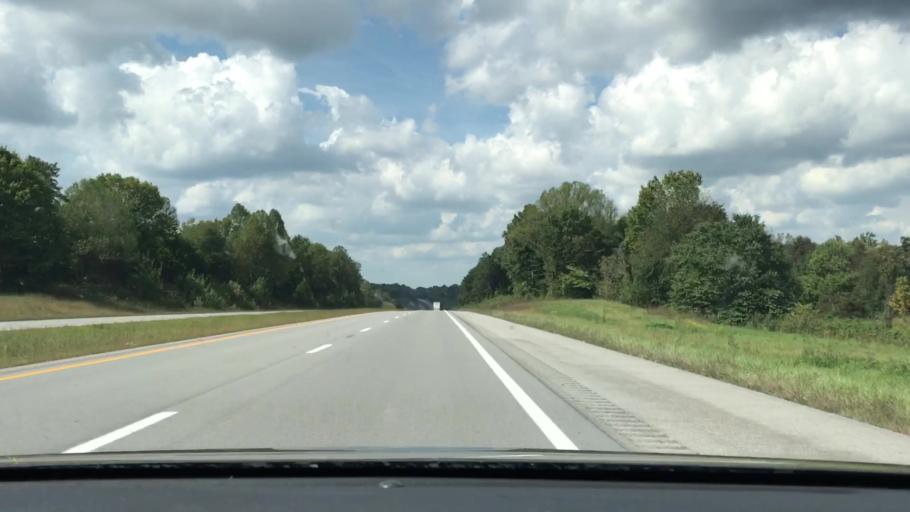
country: US
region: Kentucky
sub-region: Russell County
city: Russell Springs
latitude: 37.0549
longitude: -85.1663
